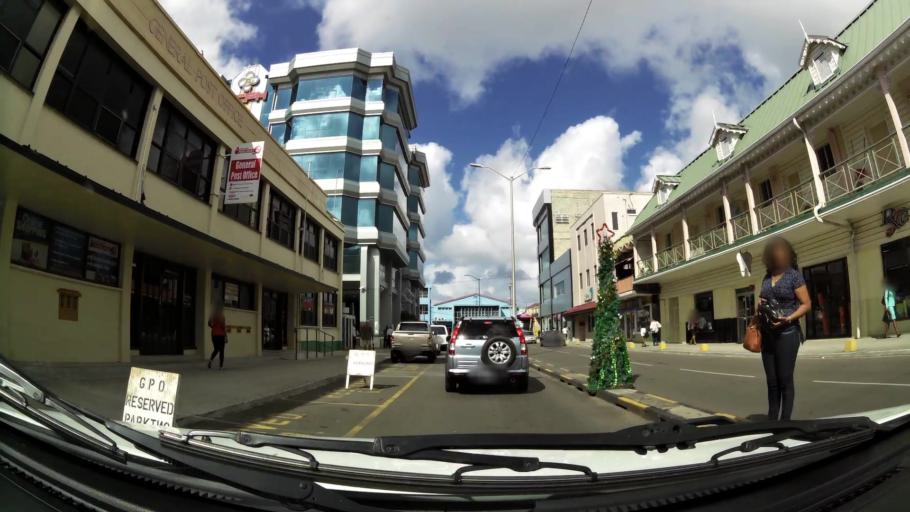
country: LC
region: Castries Quarter
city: Castries
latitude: 14.0102
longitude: -60.9916
